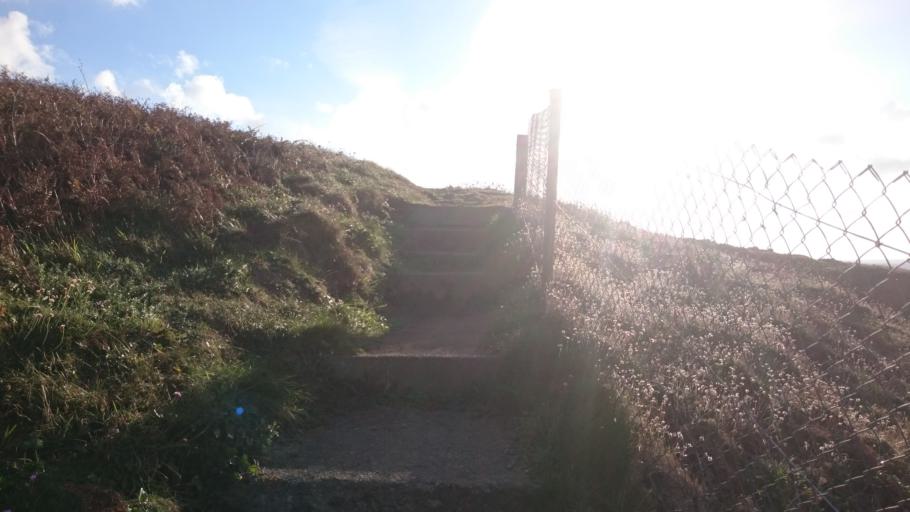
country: GG
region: St Peter Port
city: Saint Peter Port
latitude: 49.4252
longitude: -2.6627
